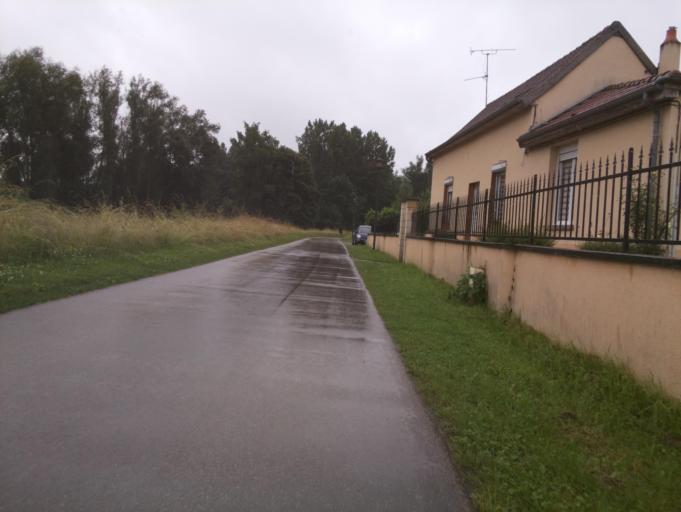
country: FR
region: Picardie
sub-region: Departement de la Somme
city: Dreuil-les-Amiens
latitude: 49.9183
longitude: 2.2307
